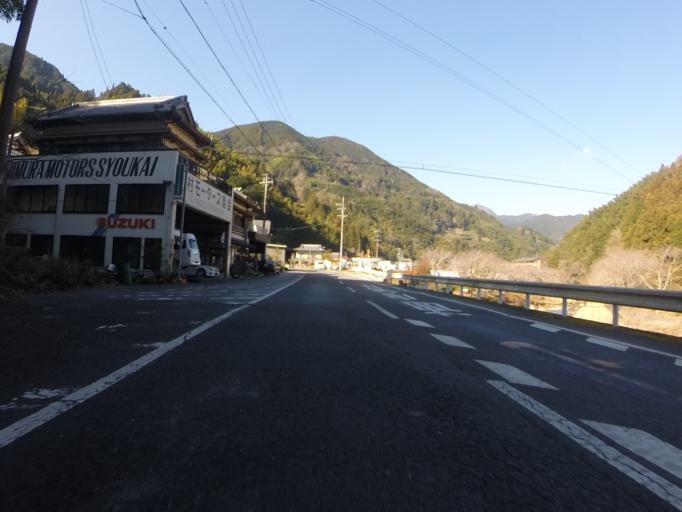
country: JP
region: Shizuoka
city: Fujinomiya
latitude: 35.1304
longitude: 138.4746
